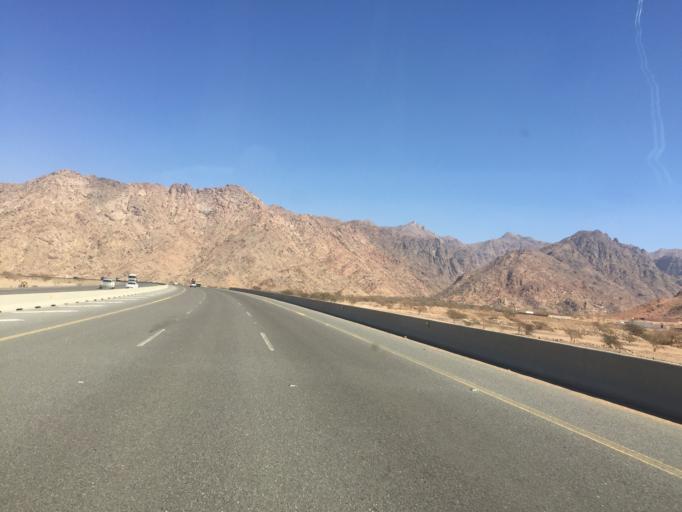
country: SA
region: Al Madinah al Munawwarah
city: Badr Hunayn
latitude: 24.0653
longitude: 39.2041
